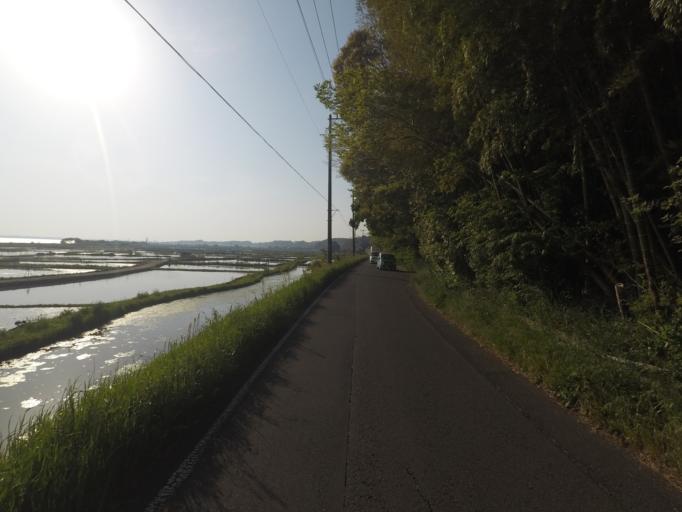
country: JP
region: Ibaraki
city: Ami
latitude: 36.0650
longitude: 140.2877
